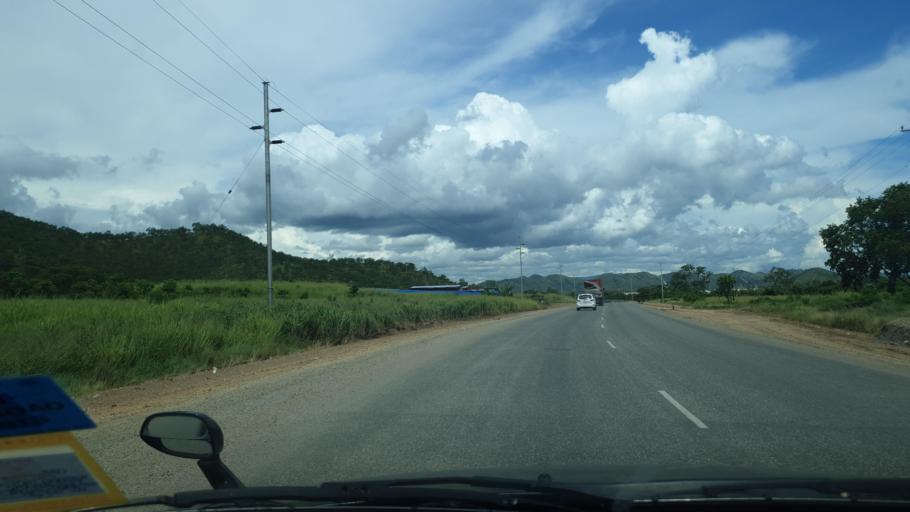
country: PG
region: National Capital
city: Port Moresby
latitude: -9.4193
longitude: 147.0888
